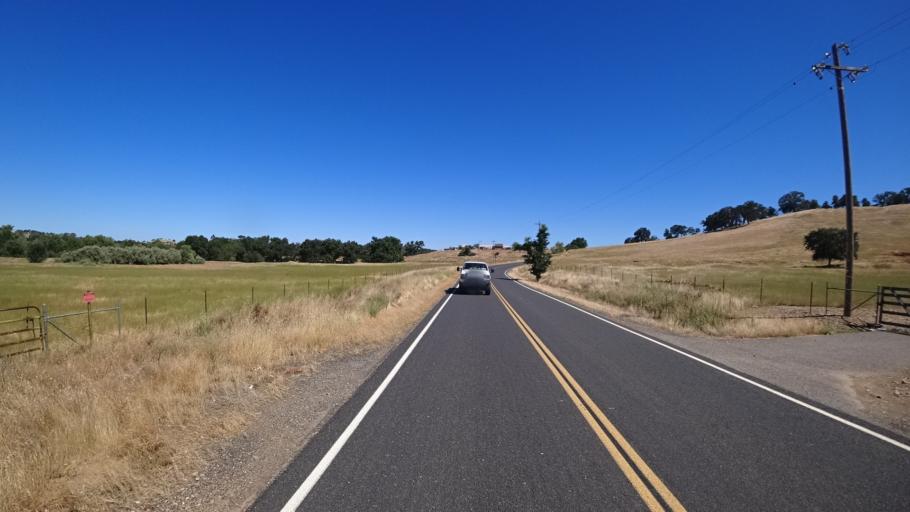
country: US
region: California
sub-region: Calaveras County
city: Rancho Calaveras
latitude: 38.0853
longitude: -120.8739
